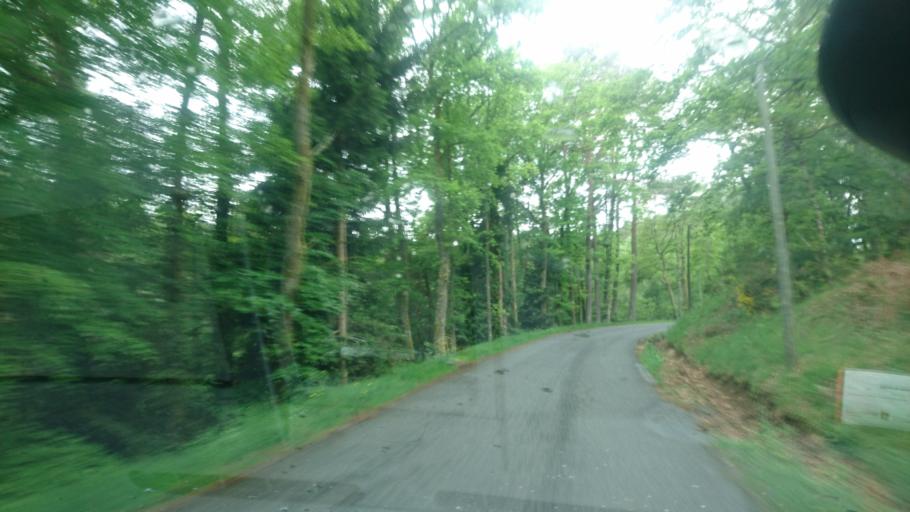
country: FR
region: Limousin
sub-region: Departement de la Haute-Vienne
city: Peyrat-le-Chateau
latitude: 45.8311
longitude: 1.8606
